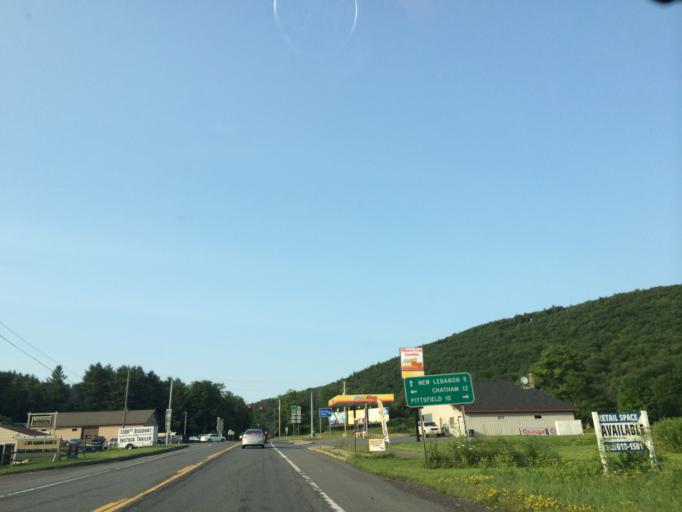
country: US
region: Massachusetts
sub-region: Berkshire County
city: Richmond
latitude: 42.3930
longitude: -73.4129
